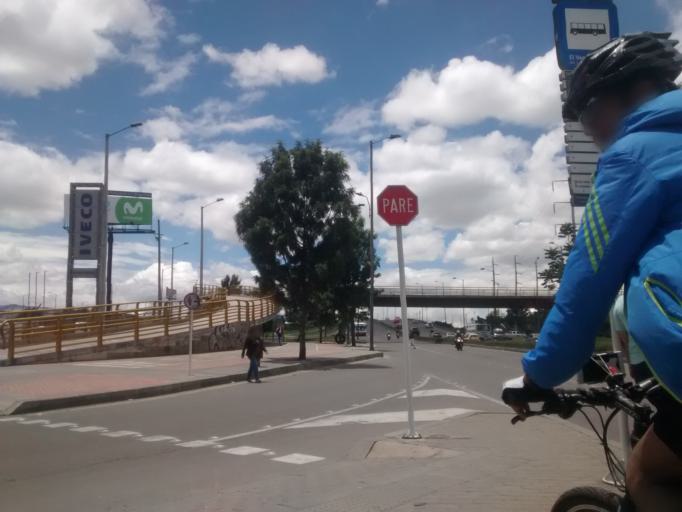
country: CO
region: Bogota D.C.
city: Bogota
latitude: 4.6611
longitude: -74.1341
